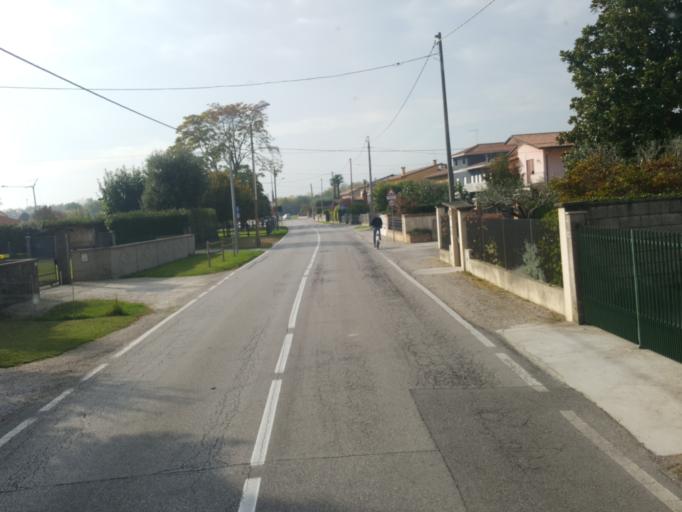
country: IT
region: Veneto
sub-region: Provincia di Vicenza
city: Rossano Veneto
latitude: 45.7170
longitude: 11.8157
